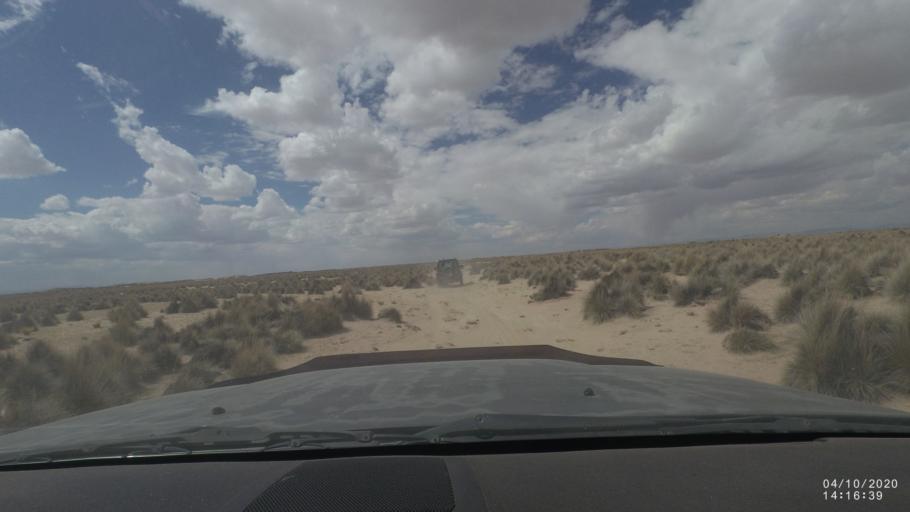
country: BO
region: Oruro
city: Poopo
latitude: -18.6898
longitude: -67.4524
